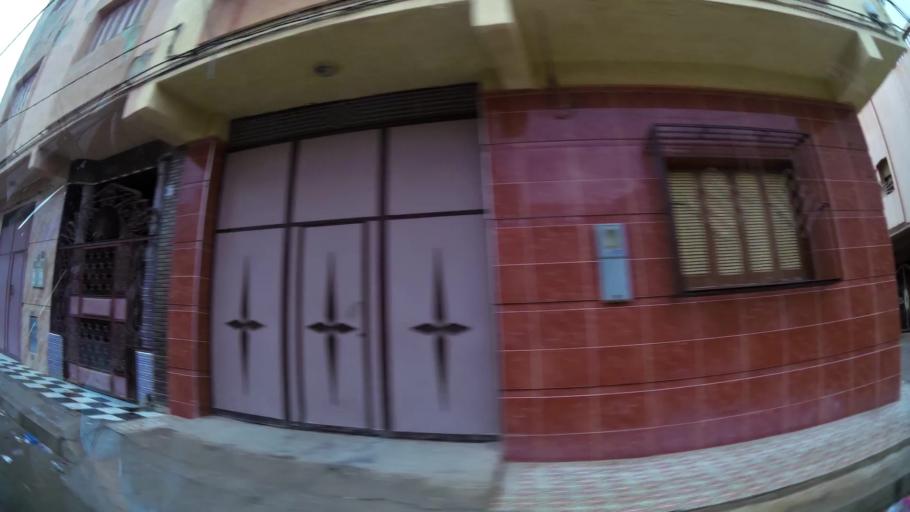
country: MA
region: Oriental
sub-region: Nador
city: Nador
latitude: 35.1614
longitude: -2.9532
